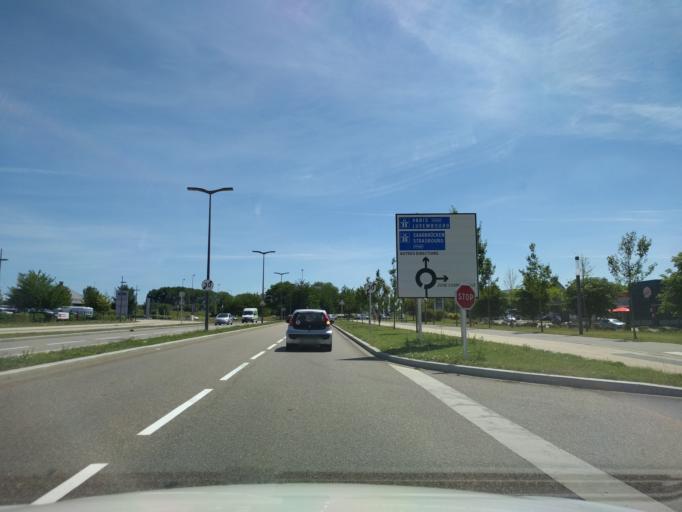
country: FR
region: Lorraine
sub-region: Departement de la Moselle
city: Peltre
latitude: 49.1075
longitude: 6.2292
